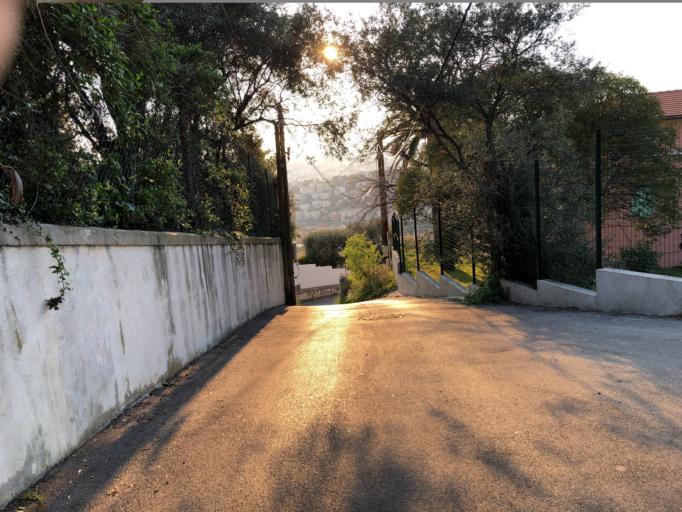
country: FR
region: Provence-Alpes-Cote d'Azur
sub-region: Departement des Alpes-Maritimes
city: Villefranche-sur-Mer
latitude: 43.7195
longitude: 7.2983
